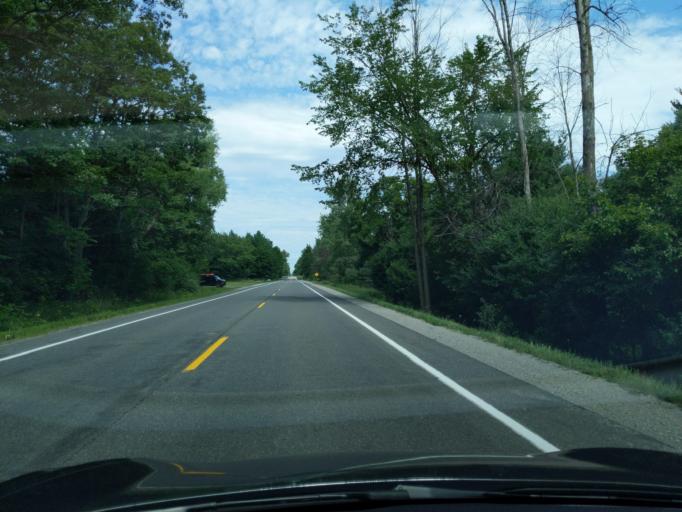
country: US
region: Michigan
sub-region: Midland County
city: Midland
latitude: 43.5909
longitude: -84.3693
